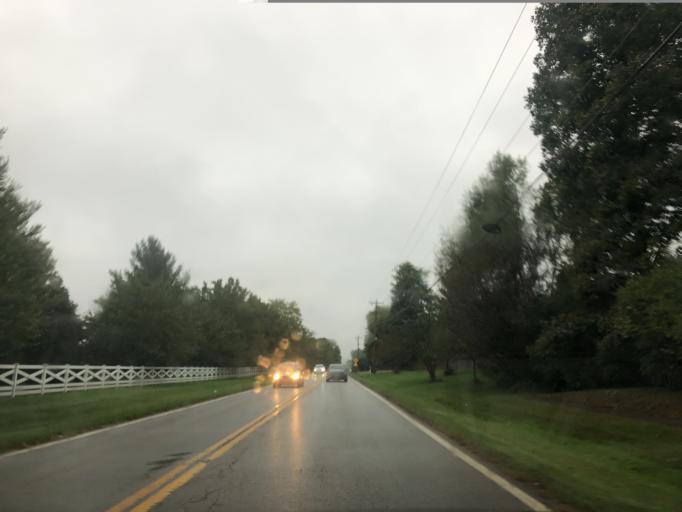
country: US
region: Ohio
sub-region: Clermont County
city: Mulberry
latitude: 39.2172
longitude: -84.2434
